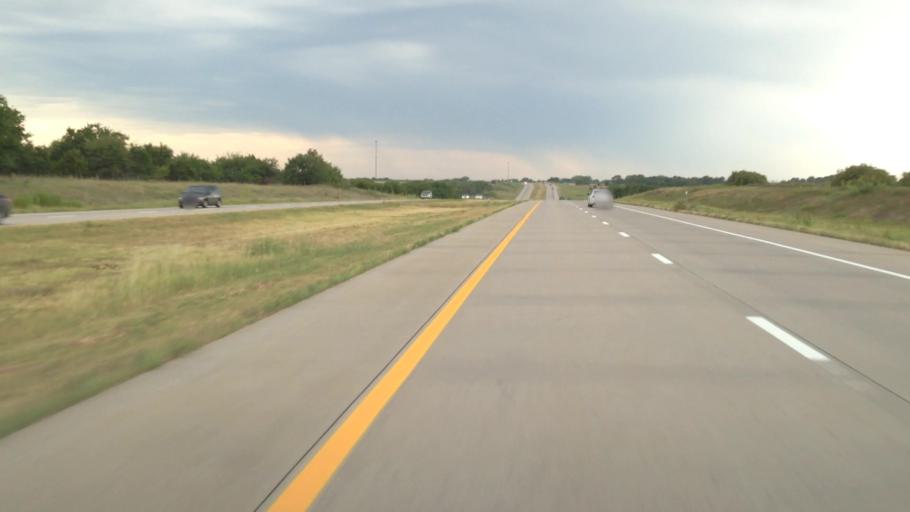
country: US
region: Kansas
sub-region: Franklin County
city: Ottawa
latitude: 38.5001
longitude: -95.4460
